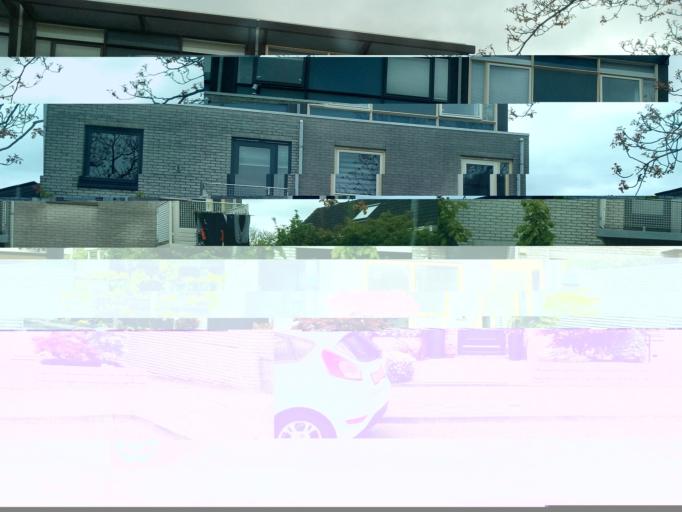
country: NL
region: South Holland
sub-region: Gemeente Alphen aan den Rijn
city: Alphen aan den Rijn
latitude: 52.1185
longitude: 4.6718
